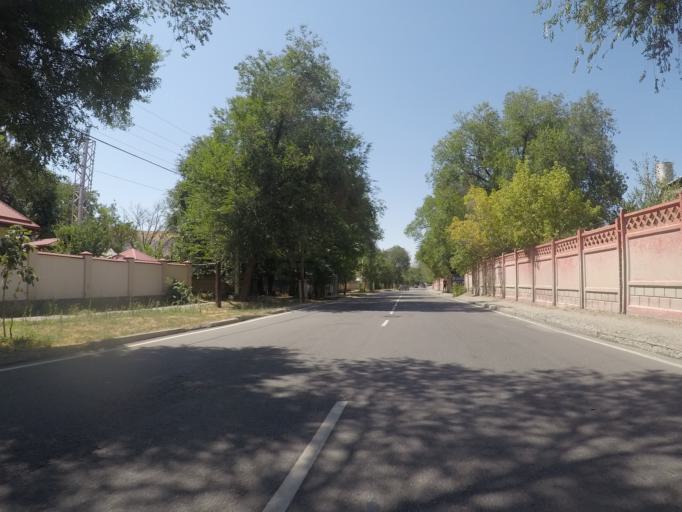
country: KG
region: Chuy
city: Bishkek
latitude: 42.8041
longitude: 74.5776
